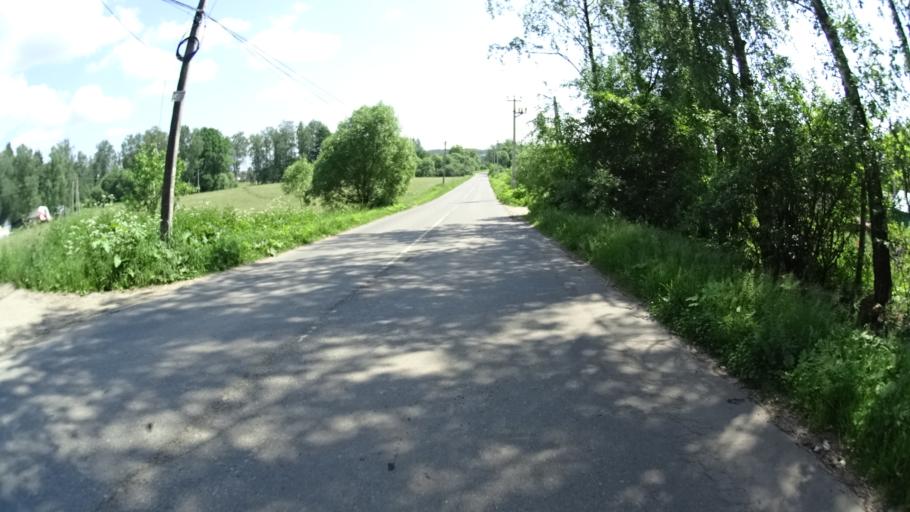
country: RU
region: Moskovskaya
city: Lesnoy
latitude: 56.0696
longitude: 37.9911
